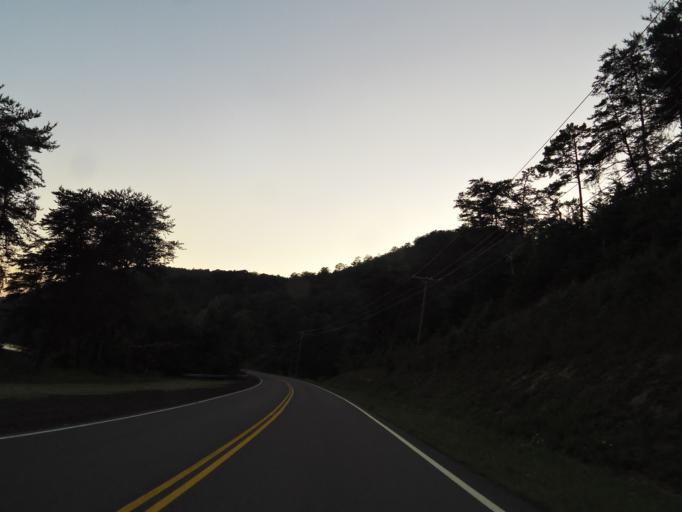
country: US
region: Tennessee
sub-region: Loudon County
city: Greenback
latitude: 35.5514
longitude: -84.0264
